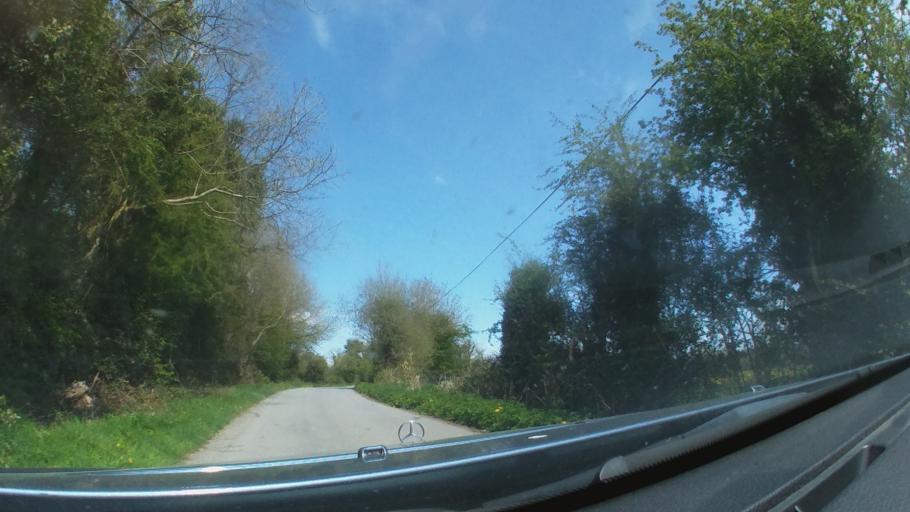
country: IE
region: Leinster
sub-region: Kilkenny
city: Callan
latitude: 52.6234
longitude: -7.4649
